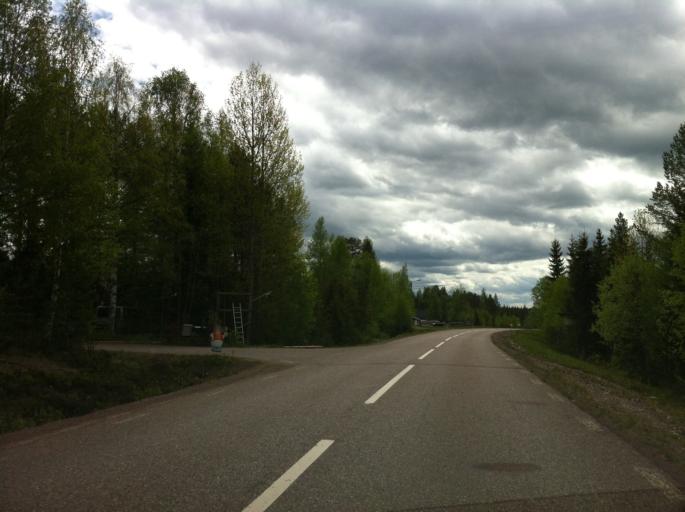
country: NO
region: Hedmark
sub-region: Trysil
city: Innbygda
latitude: 61.5174
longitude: 13.0830
